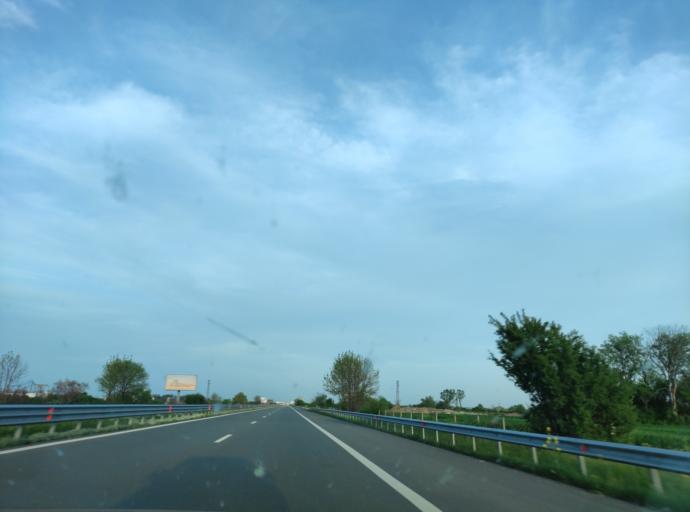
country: BG
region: Plovdiv
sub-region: Obshtina Rakovski
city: Rakovski
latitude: 42.2138
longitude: 25.0693
